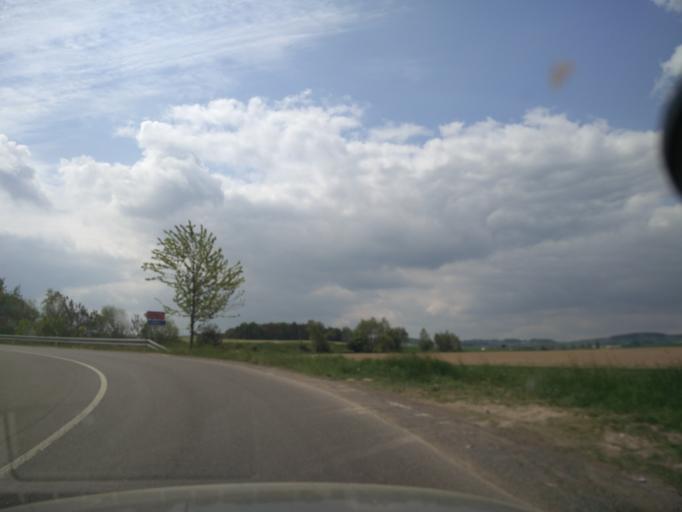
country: CZ
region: Central Bohemia
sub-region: Okres Pribram
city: Pribram
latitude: 49.7061
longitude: 14.0872
